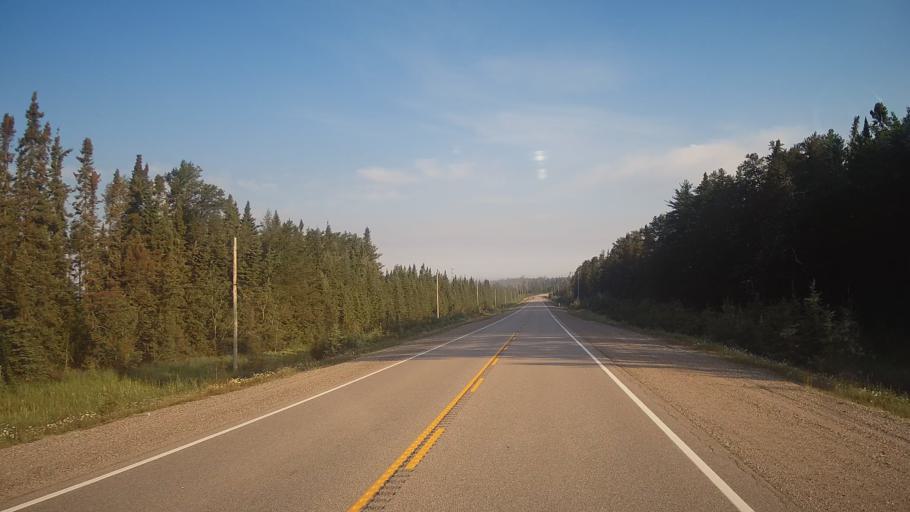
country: CA
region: Ontario
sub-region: Rainy River District
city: Atikokan
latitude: 49.3833
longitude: -91.5904
